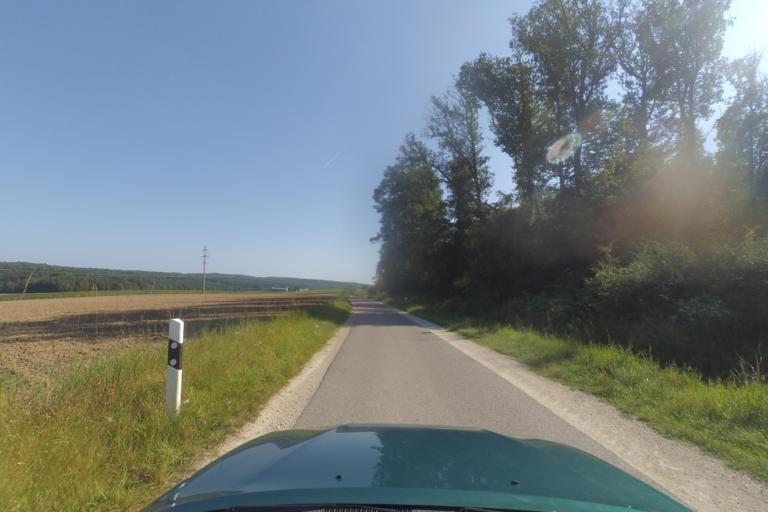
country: DE
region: Bavaria
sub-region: Swabia
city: Harburg
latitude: 48.7813
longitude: 10.7191
